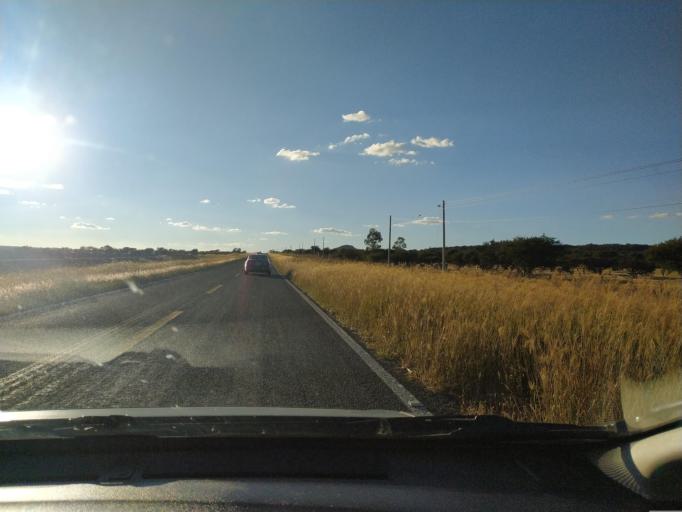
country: MX
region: Jalisco
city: San Diego de Alejandria
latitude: 21.0051
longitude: -102.0688
